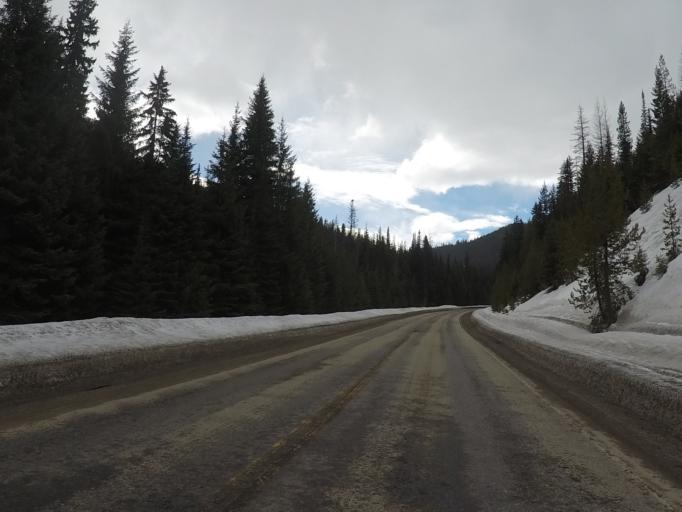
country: US
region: Montana
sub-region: Missoula County
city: Frenchtown
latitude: 46.6661
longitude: -114.5782
